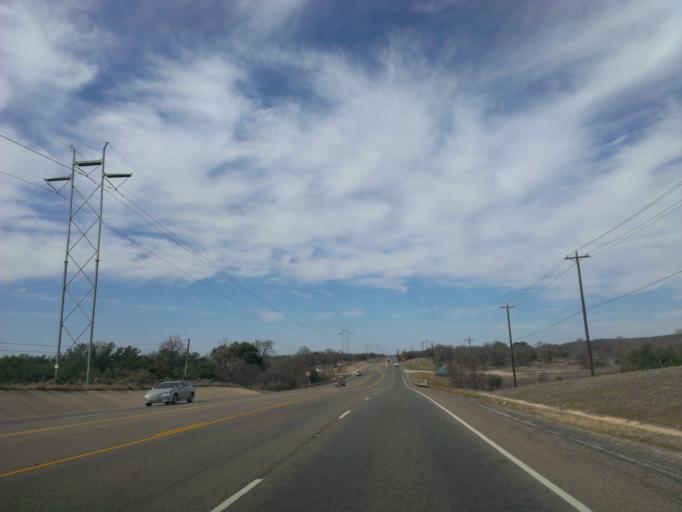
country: US
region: Texas
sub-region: Burnet County
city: Granite Shoals
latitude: 30.6159
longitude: -98.3884
